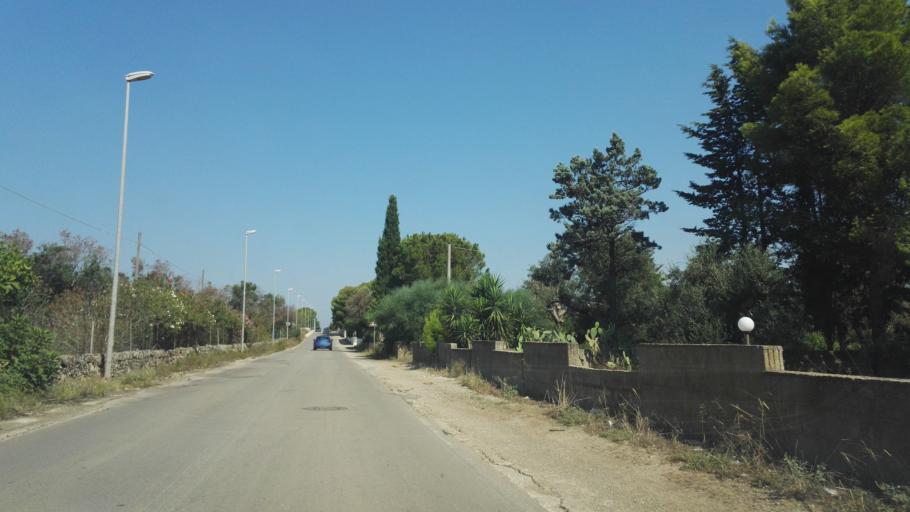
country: IT
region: Apulia
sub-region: Provincia di Lecce
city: Nardo
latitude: 40.1421
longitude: 18.0112
